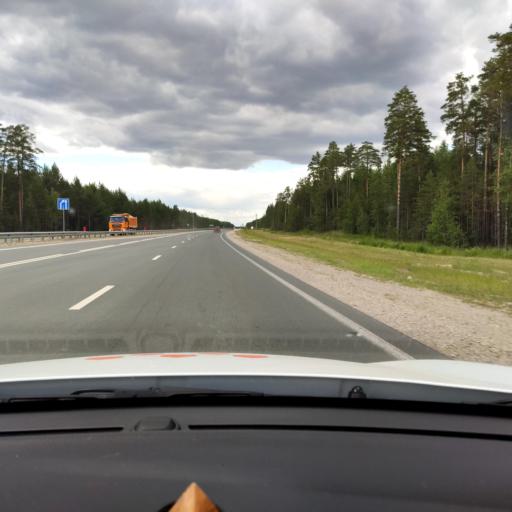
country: RU
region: Mariy-El
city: Surok
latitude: 56.4528
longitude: 48.0989
